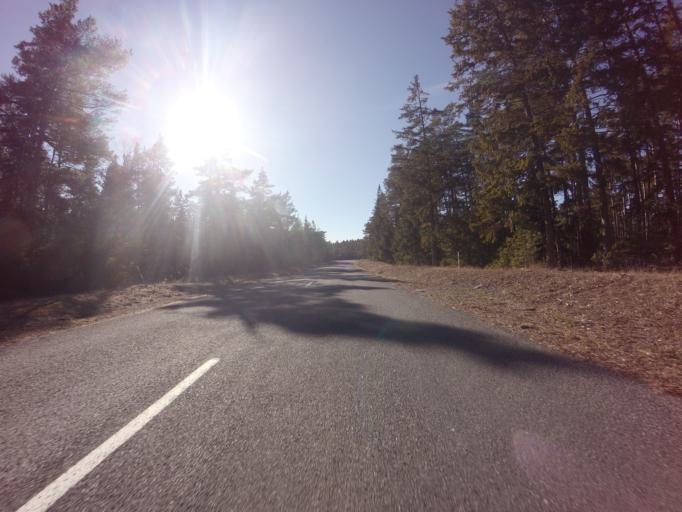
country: EE
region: Saare
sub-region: Kuressaare linn
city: Kuressaare
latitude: 58.5136
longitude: 22.3188
